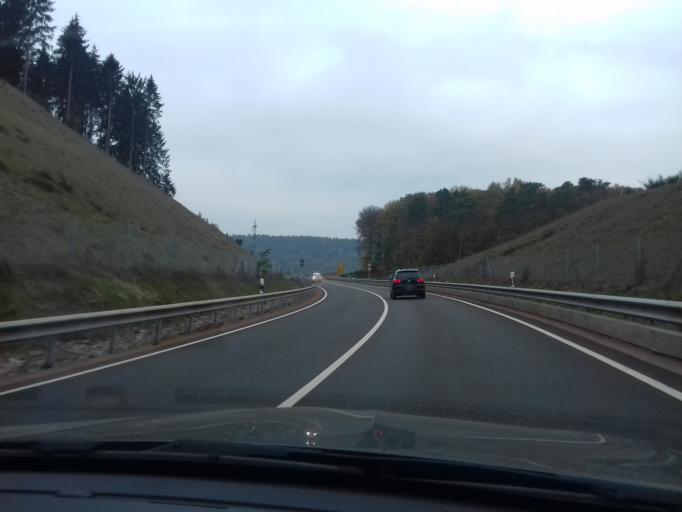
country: DE
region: Rheinland-Pfalz
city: Wawern
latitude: 49.6698
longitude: 6.5401
